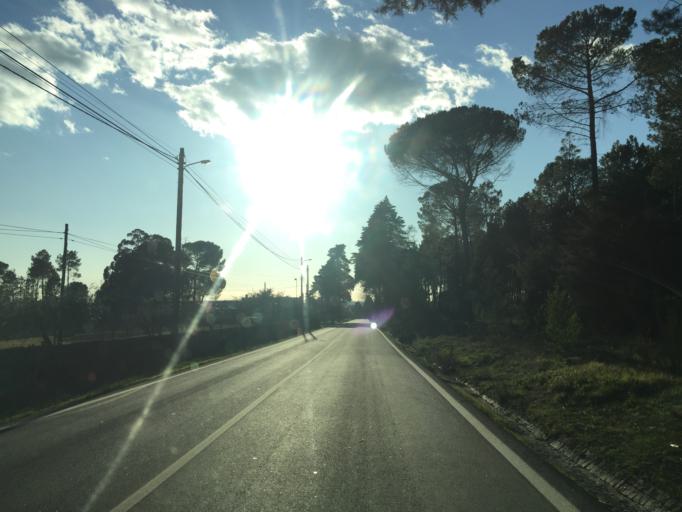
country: PT
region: Viseu
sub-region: Nelas
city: Nelas
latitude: 40.5198
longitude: -7.8705
